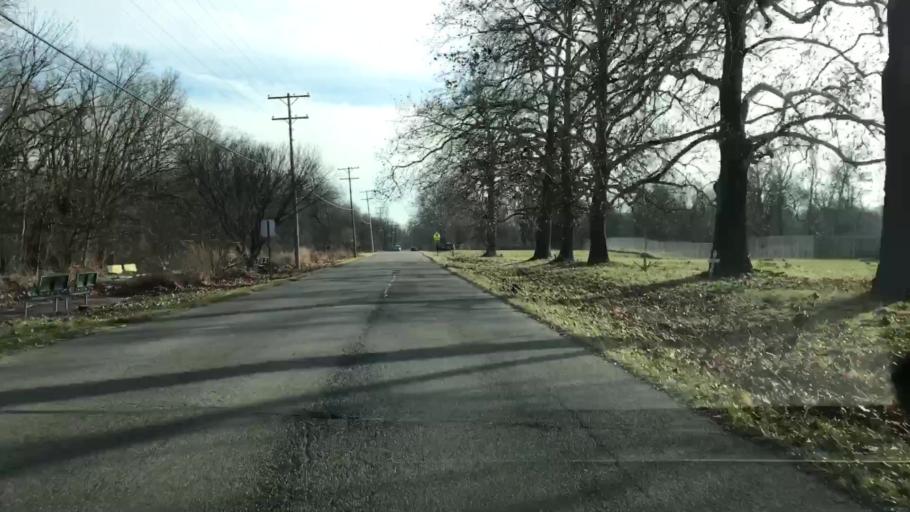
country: US
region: Ohio
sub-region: Greene County
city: Yellow Springs
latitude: 39.7972
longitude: -83.8847
